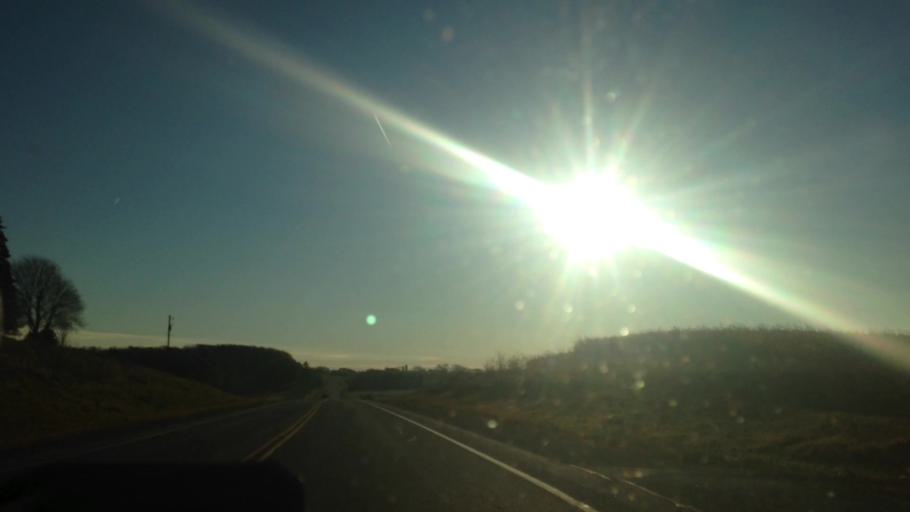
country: US
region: Wisconsin
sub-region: Dodge County
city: Theresa
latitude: 43.4358
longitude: -88.4711
